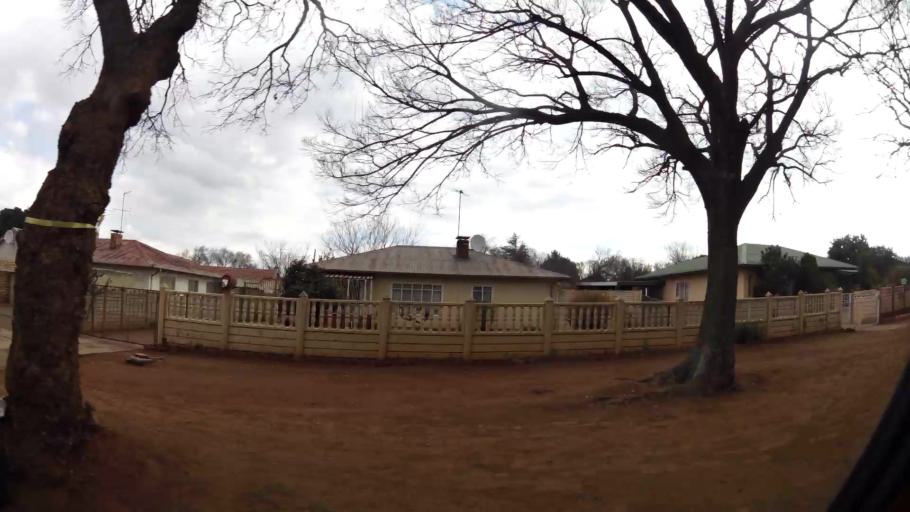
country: ZA
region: Gauteng
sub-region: Sedibeng District Municipality
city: Vanderbijlpark
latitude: -26.6995
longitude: 27.8227
